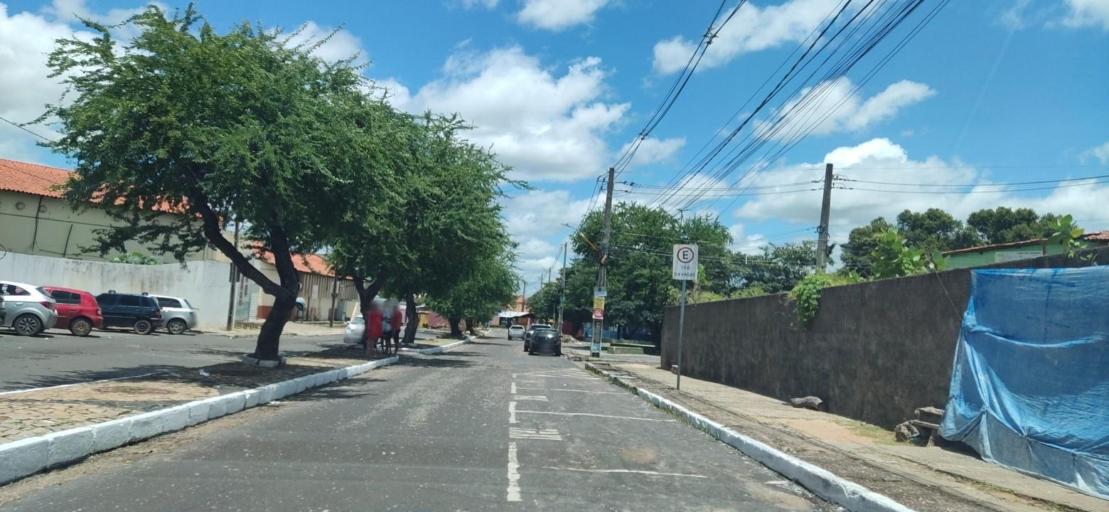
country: BR
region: Piaui
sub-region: Teresina
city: Teresina
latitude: -5.1480
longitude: -42.7825
